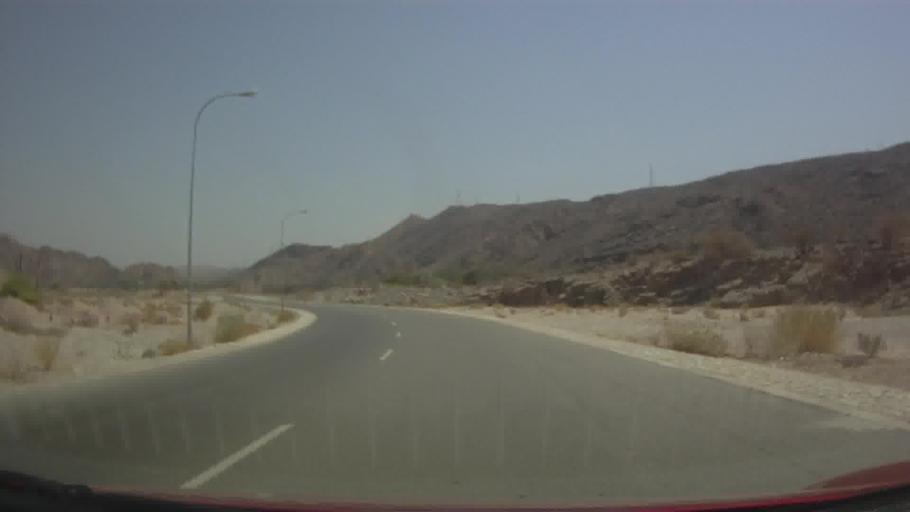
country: OM
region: Muhafazat Masqat
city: Muscat
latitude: 23.5102
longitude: 58.6358
